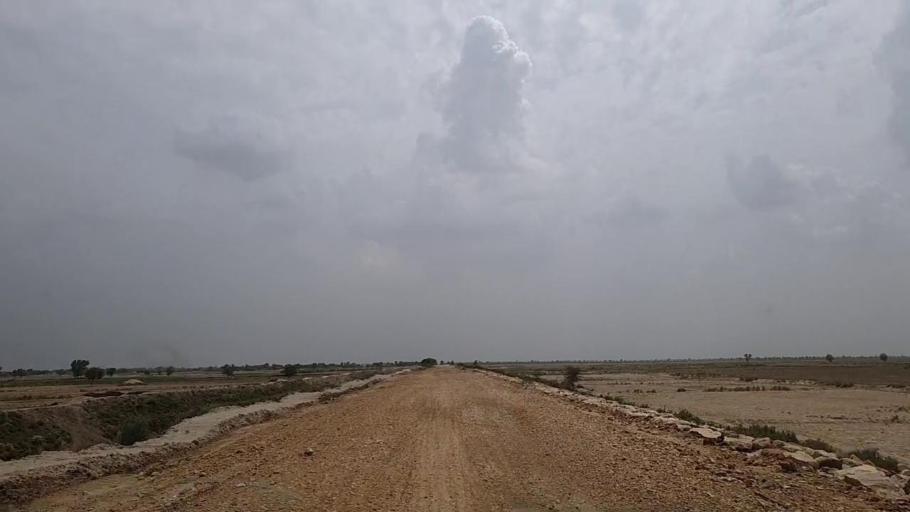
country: PK
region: Sindh
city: Johi
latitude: 26.7451
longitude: 67.5875
